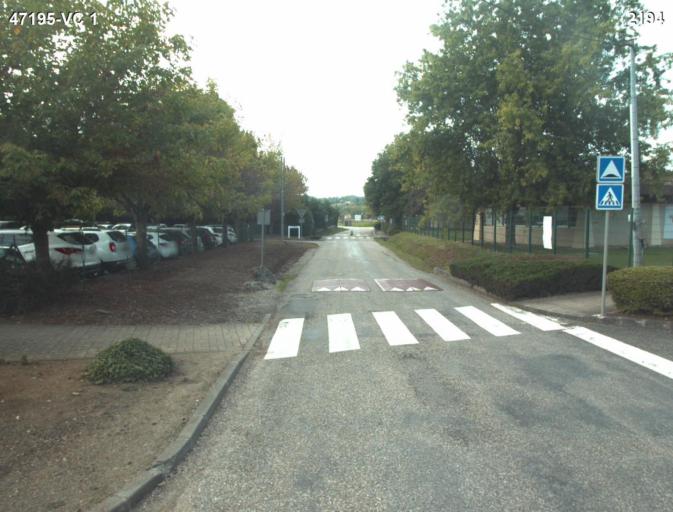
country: FR
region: Aquitaine
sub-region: Departement du Lot-et-Garonne
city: Nerac
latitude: 44.1216
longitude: 0.3567
